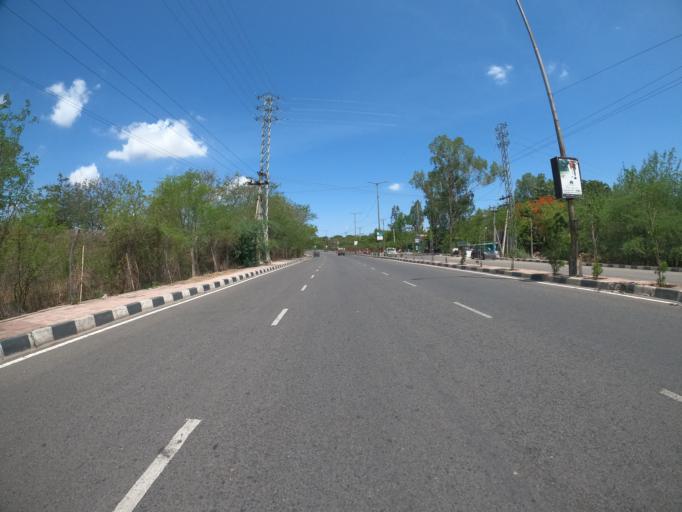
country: IN
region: Telangana
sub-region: Hyderabad
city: Hyderabad
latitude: 17.3511
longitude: 78.3661
